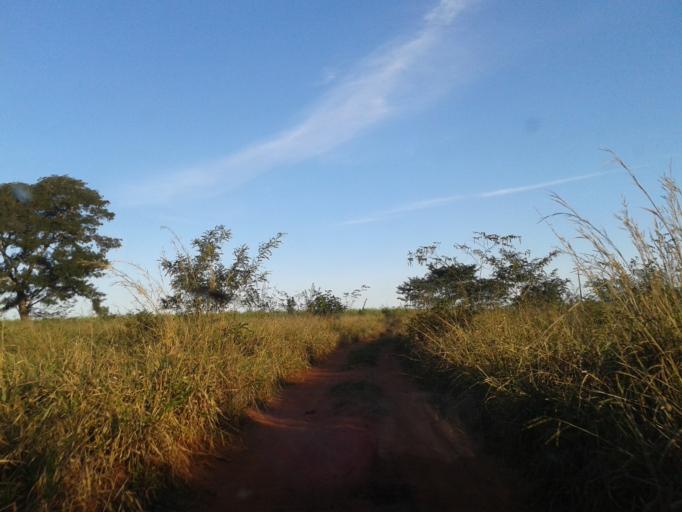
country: BR
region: Minas Gerais
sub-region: Santa Vitoria
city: Santa Vitoria
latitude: -19.0024
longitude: -50.3846
